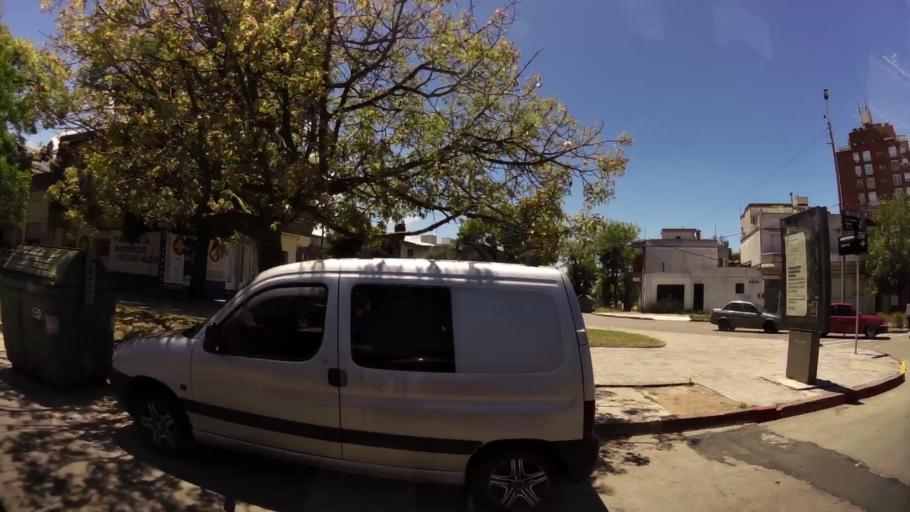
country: UY
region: Montevideo
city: Montevideo
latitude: -34.8957
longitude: -56.1478
